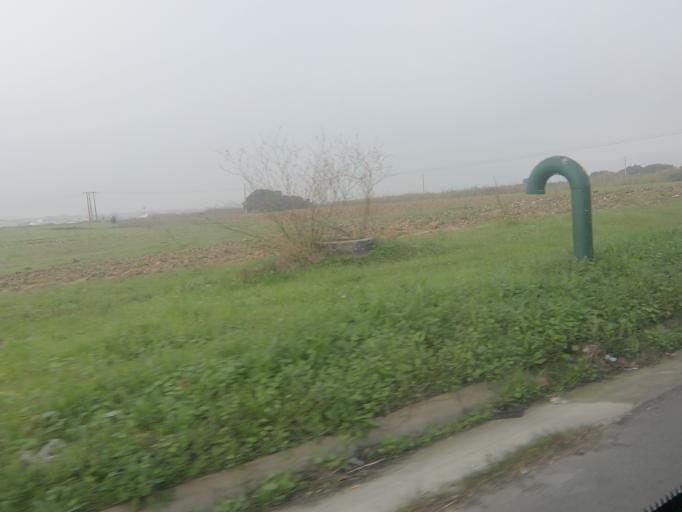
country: PT
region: Setubal
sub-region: Montijo
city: Montijo
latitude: 38.6923
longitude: -8.9498
